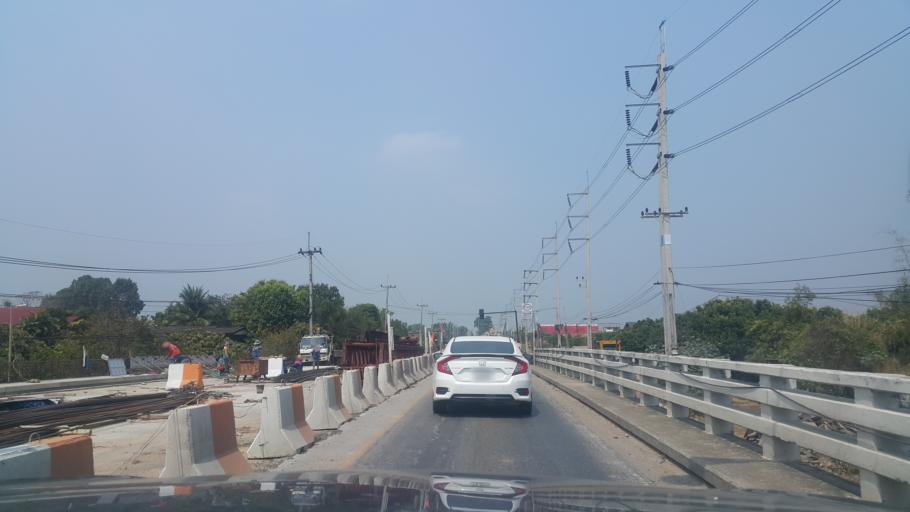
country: TH
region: Lamphun
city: Pa Sang
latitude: 18.4715
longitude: 98.9551
